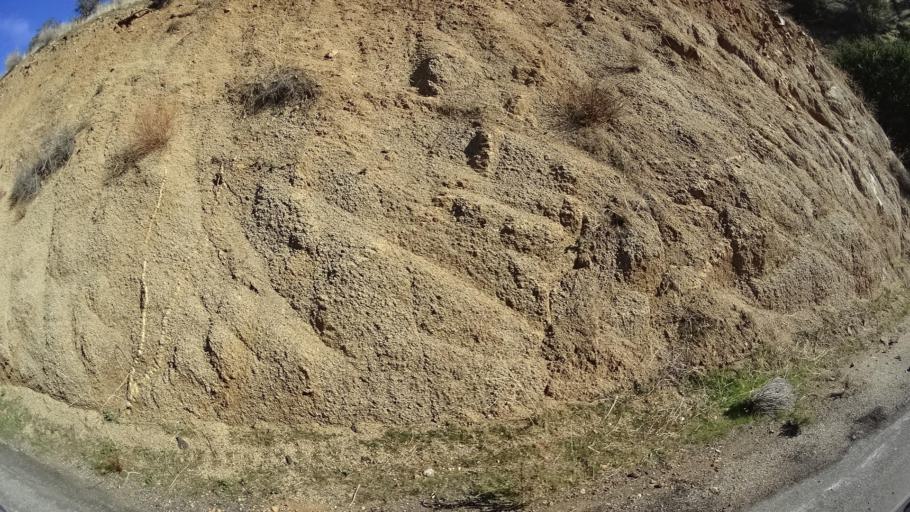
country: US
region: California
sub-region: Kern County
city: Bodfish
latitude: 35.5812
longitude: -118.5225
